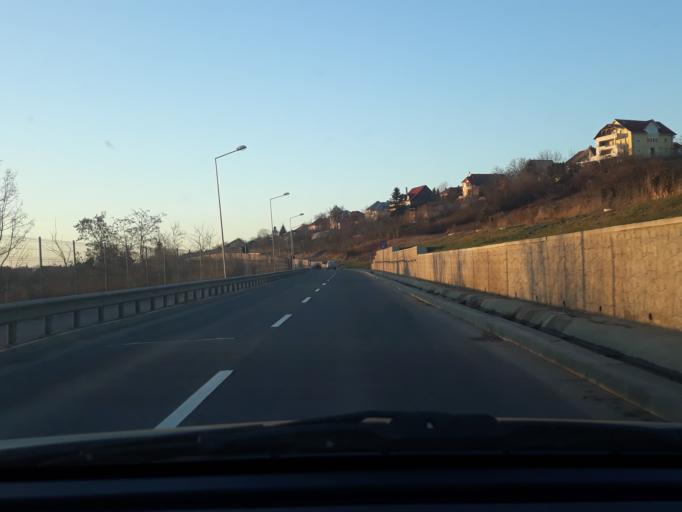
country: RO
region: Bihor
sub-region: Comuna Biharea
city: Oradea
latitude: 47.0579
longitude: 21.9480
